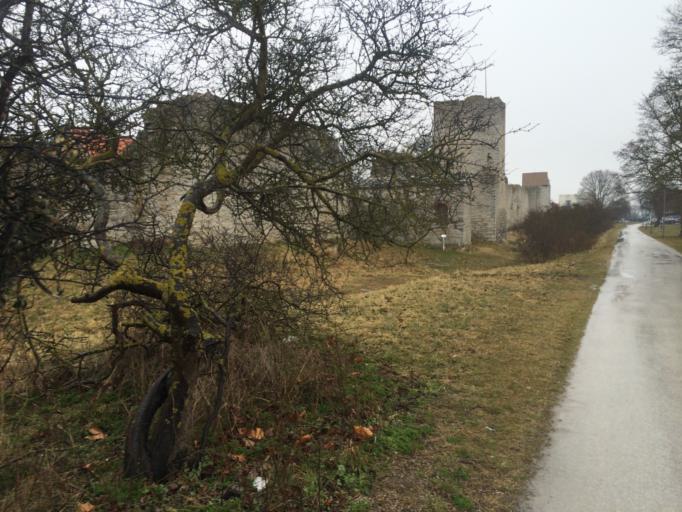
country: SE
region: Gotland
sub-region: Gotland
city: Visby
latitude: 57.6364
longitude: 18.2958
